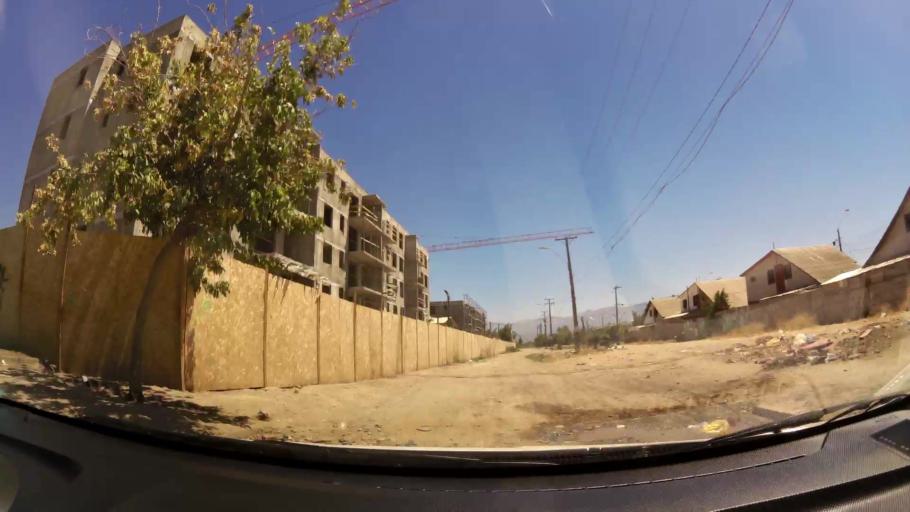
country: CL
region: O'Higgins
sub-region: Provincia de Cachapoal
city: Rancagua
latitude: -34.1623
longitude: -70.6988
